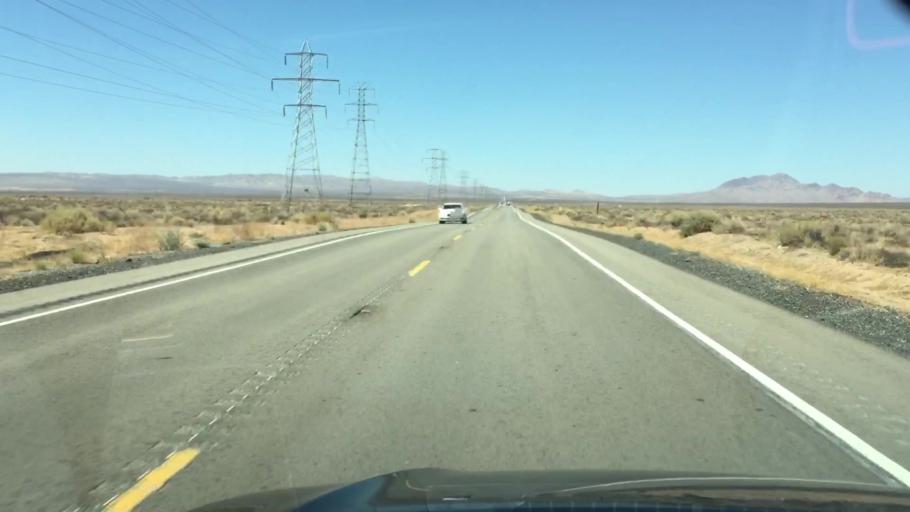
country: US
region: California
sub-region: Kern County
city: Boron
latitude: 35.1808
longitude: -117.5941
